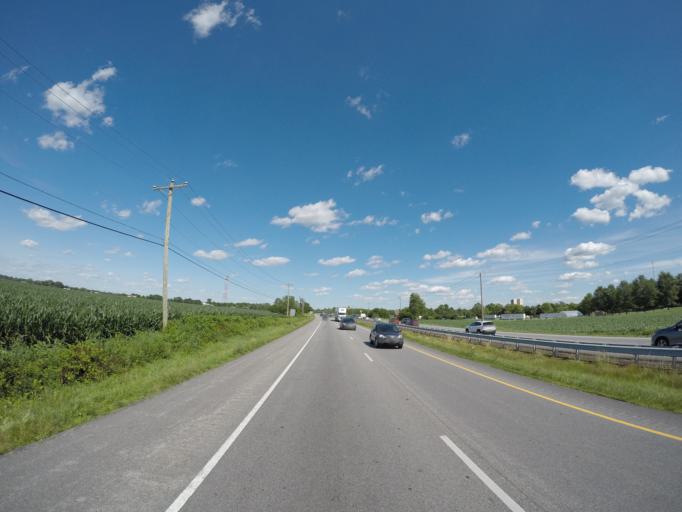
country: US
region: Maryland
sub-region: Queen Anne's County
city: Centreville
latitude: 38.9565
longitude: -76.0859
